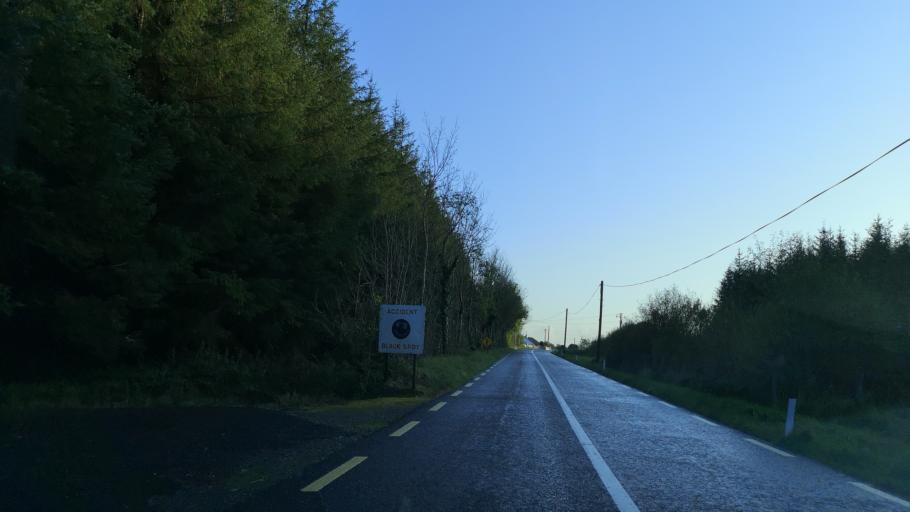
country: IE
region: Connaught
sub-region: Roscommon
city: Castlerea
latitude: 53.7197
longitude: -8.5604
